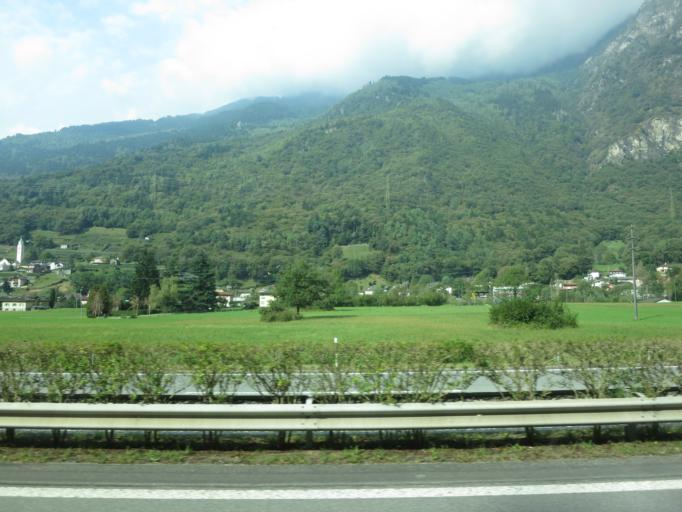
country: CH
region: Grisons
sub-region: Moesa District
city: Santa Maria in Calanca
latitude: 46.2723
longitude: 9.1753
